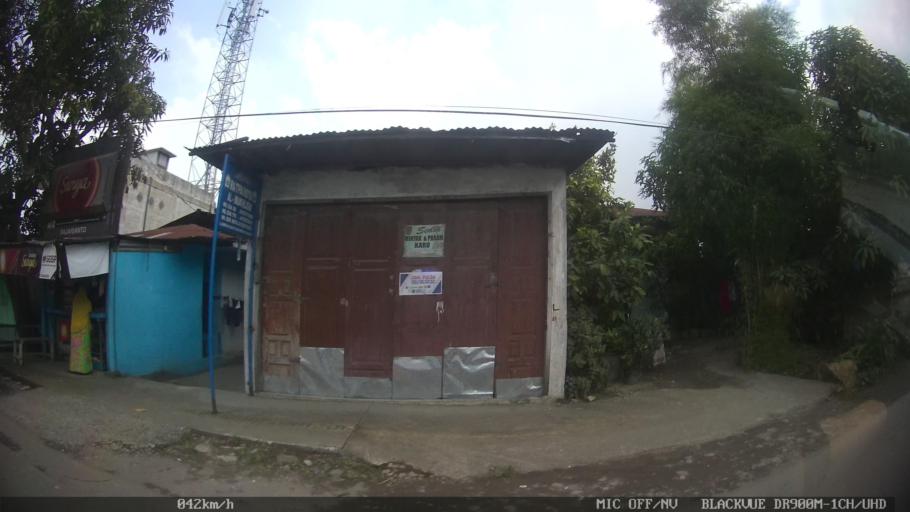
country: ID
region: North Sumatra
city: Medan
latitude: 3.6426
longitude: 98.6764
